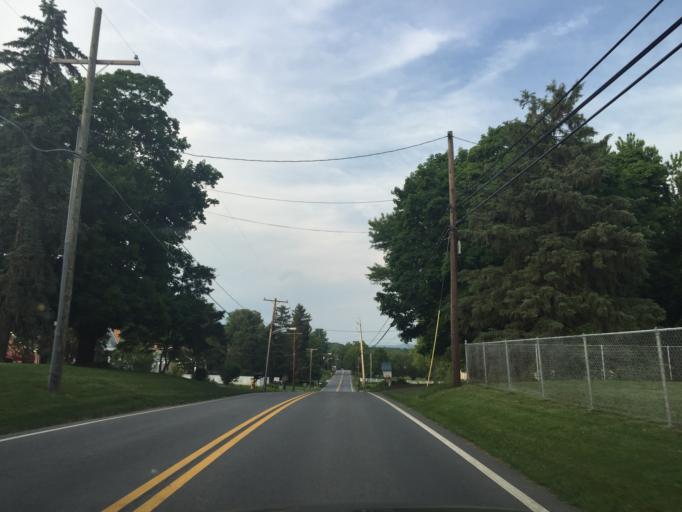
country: US
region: Maryland
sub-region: Frederick County
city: Brunswick
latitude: 39.3307
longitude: -77.6205
